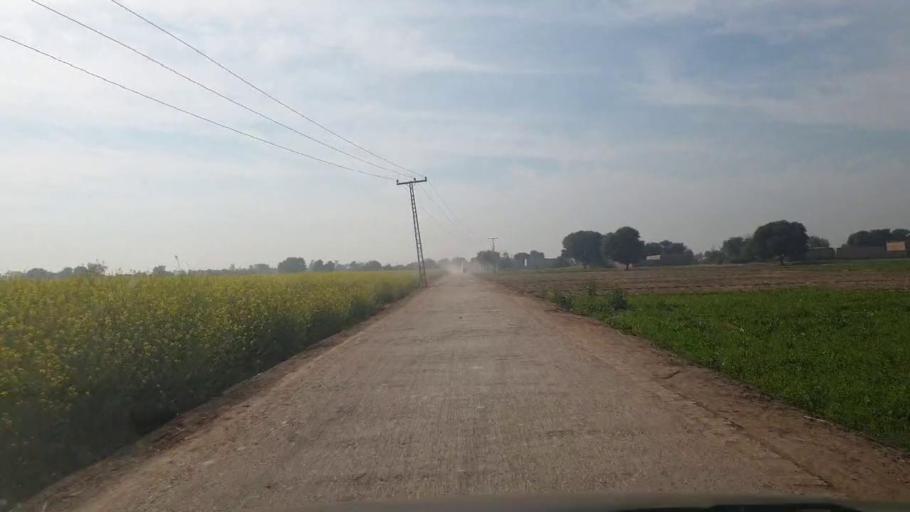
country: PK
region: Sindh
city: Shahpur Chakar
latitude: 26.1796
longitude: 68.5941
